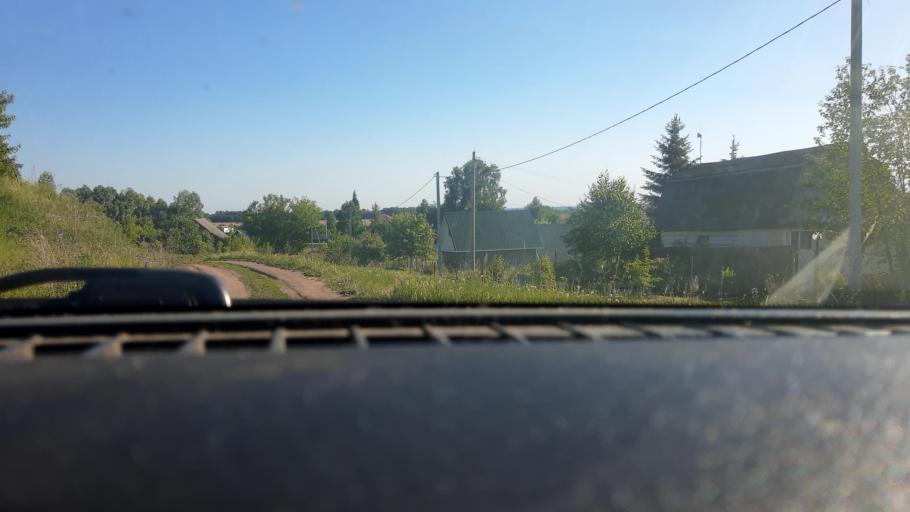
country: RU
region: Bashkortostan
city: Ulukulevo
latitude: 54.5512
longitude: 56.3223
